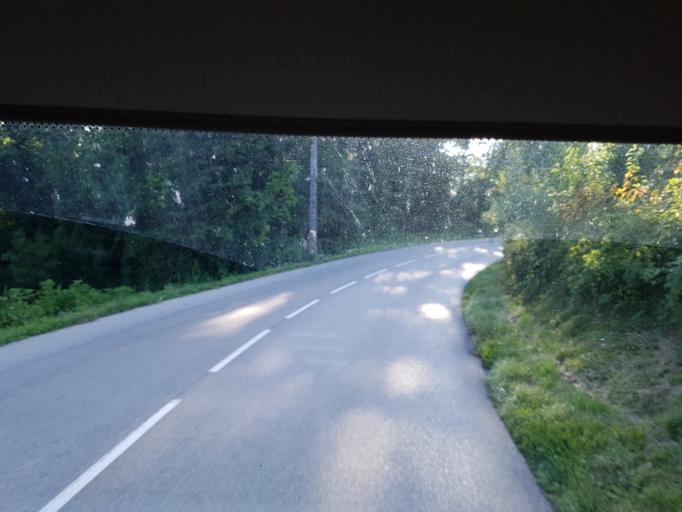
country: FR
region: Rhone-Alpes
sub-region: Departement de l'Ain
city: Priay
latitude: 46.0288
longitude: 5.3035
